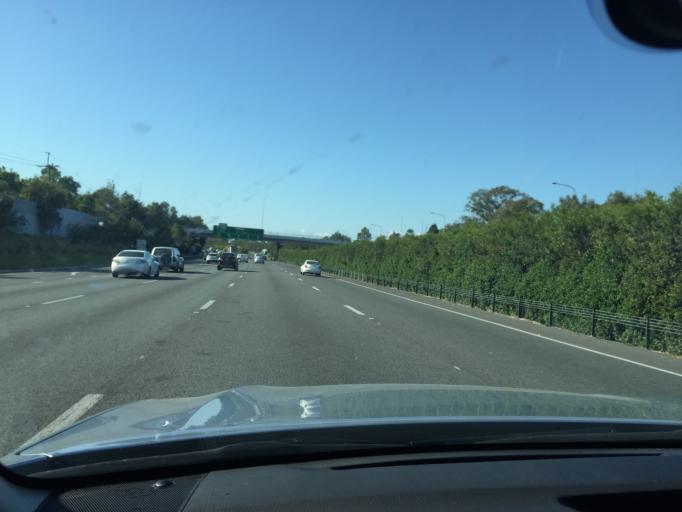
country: AU
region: Queensland
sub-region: Logan
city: Beenleigh
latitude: -27.7141
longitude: 153.2085
